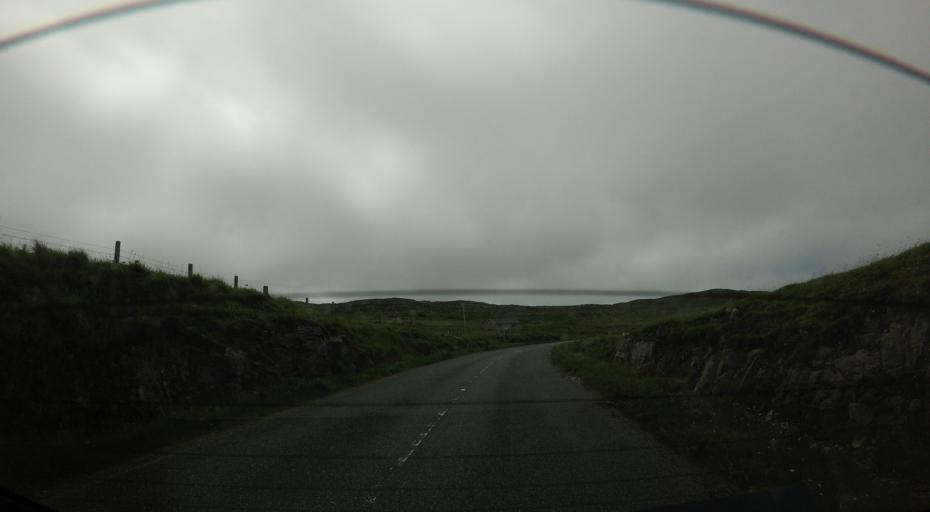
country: GB
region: Scotland
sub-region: Eilean Siar
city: Harris
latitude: 57.8645
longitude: -6.9492
